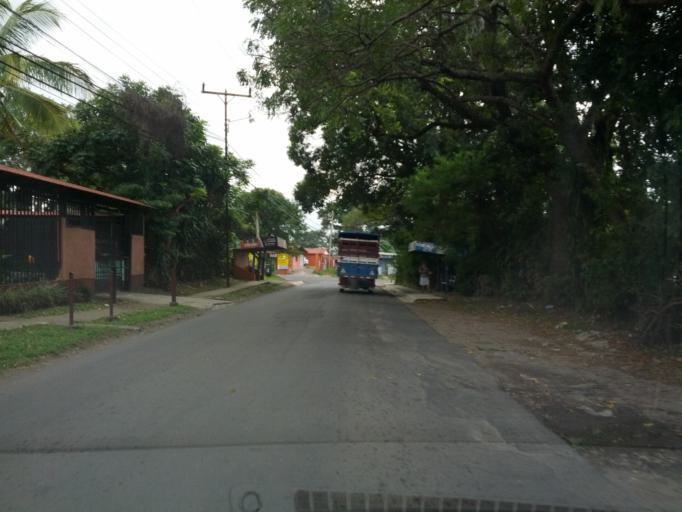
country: CR
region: Alajuela
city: Alajuela
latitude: 9.9852
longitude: -84.2224
